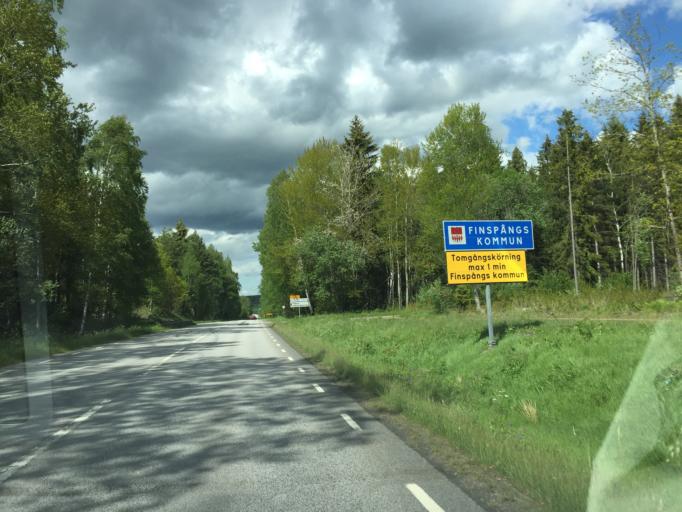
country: SE
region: OEstergoetland
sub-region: Finspangs Kommun
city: Finspang
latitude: 58.6338
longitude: 15.8210
